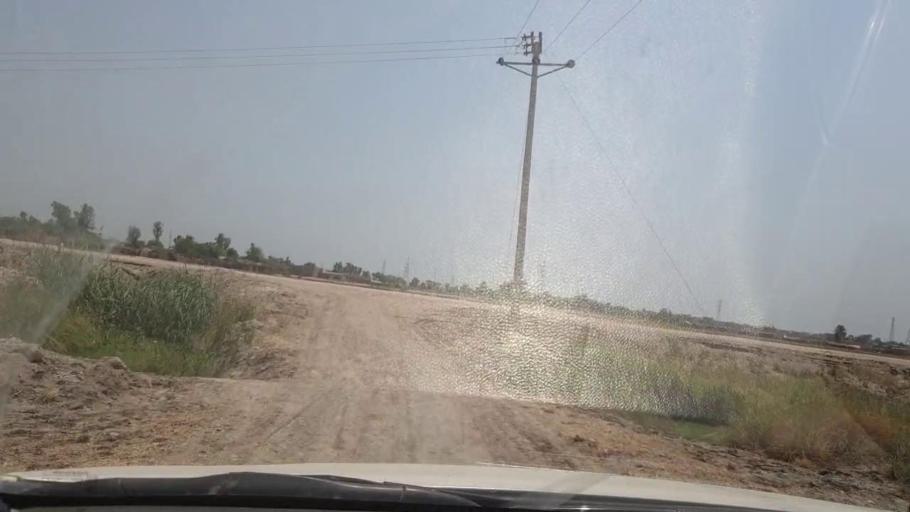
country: PK
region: Sindh
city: Lakhi
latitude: 27.8609
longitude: 68.7025
